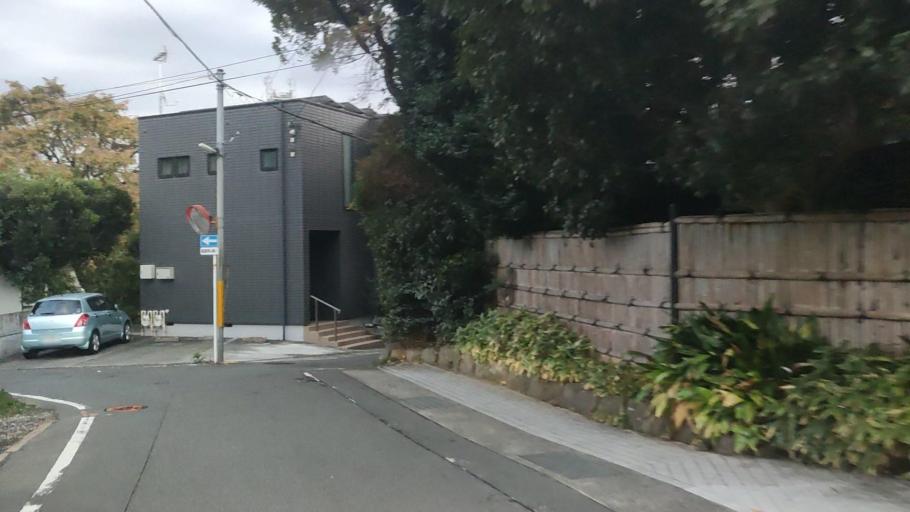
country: JP
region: Shizuoka
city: Atami
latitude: 35.0960
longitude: 139.0673
